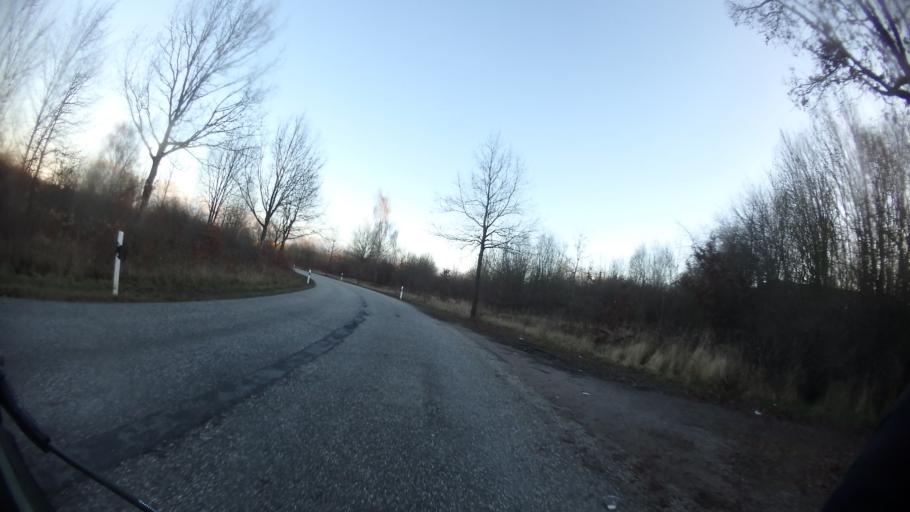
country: DE
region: Mecklenburg-Vorpommern
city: Selmsdorf
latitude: 53.9262
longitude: 10.8226
